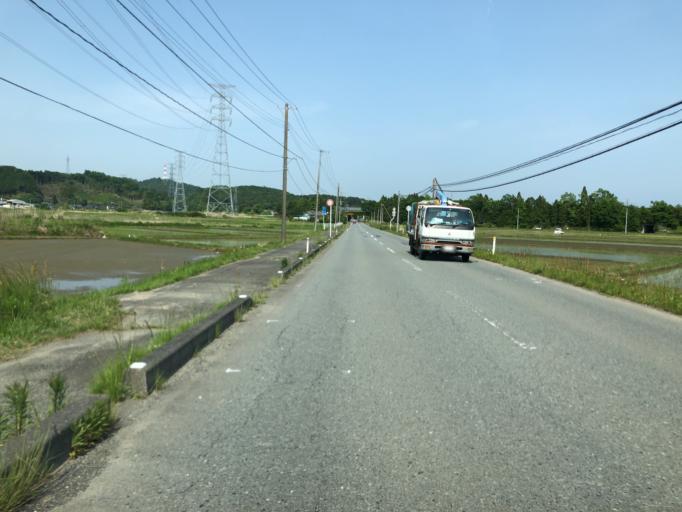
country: JP
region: Ibaraki
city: Kitaibaraki
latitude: 36.9254
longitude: 140.7583
